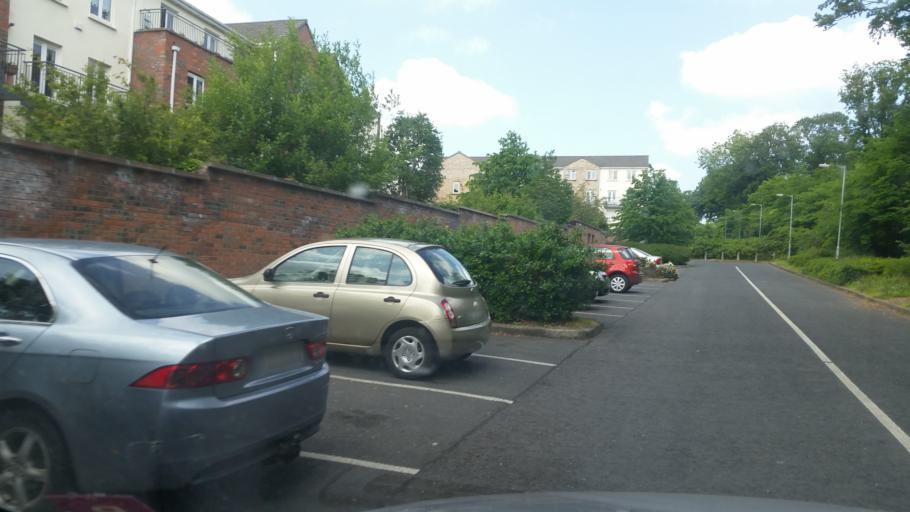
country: IE
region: Leinster
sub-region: Fingal County
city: Blanchardstown
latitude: 53.3935
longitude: -6.3750
